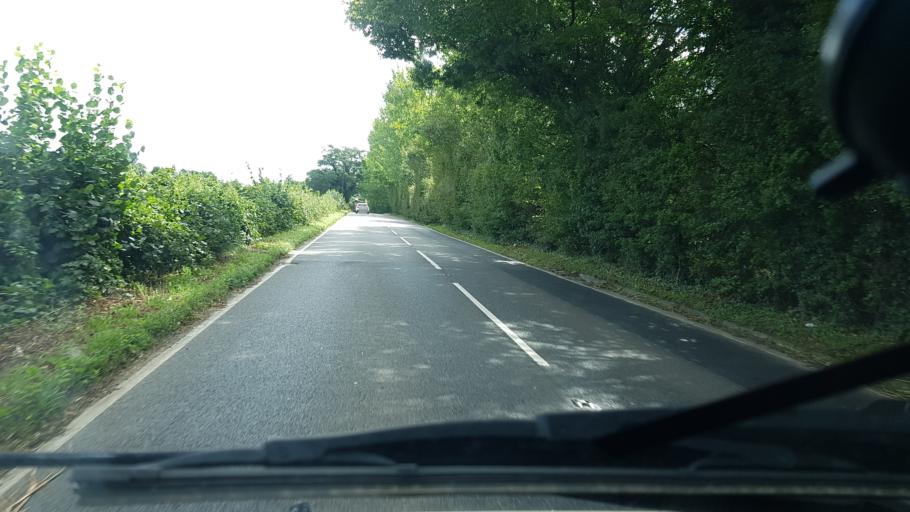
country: GB
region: England
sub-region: Surrey
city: Cranleigh
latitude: 51.1004
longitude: -0.5026
